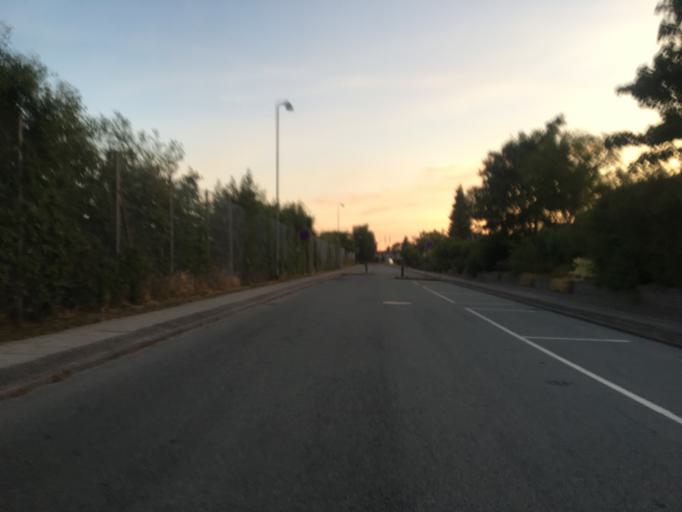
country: DK
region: Central Jutland
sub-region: Syddjurs Kommune
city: Hornslet
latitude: 56.3194
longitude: 10.3279
